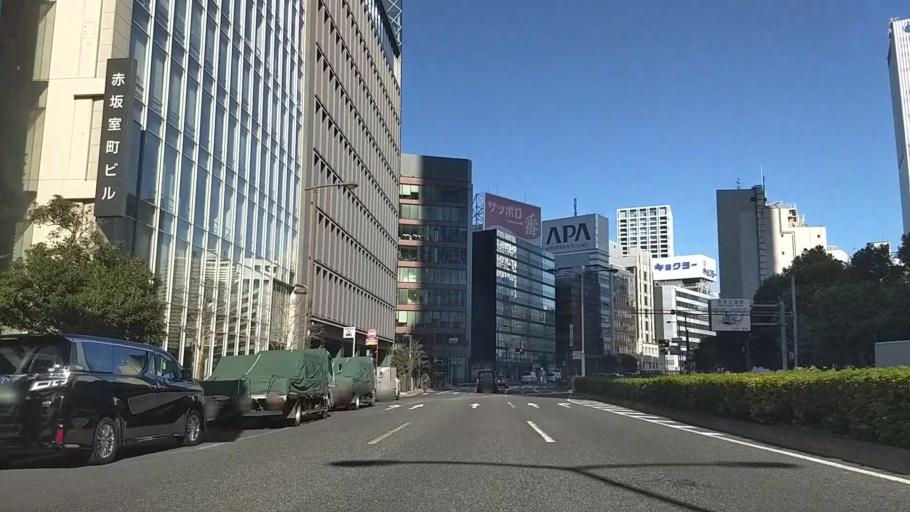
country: JP
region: Tokyo
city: Tokyo
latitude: 35.6727
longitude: 139.7402
